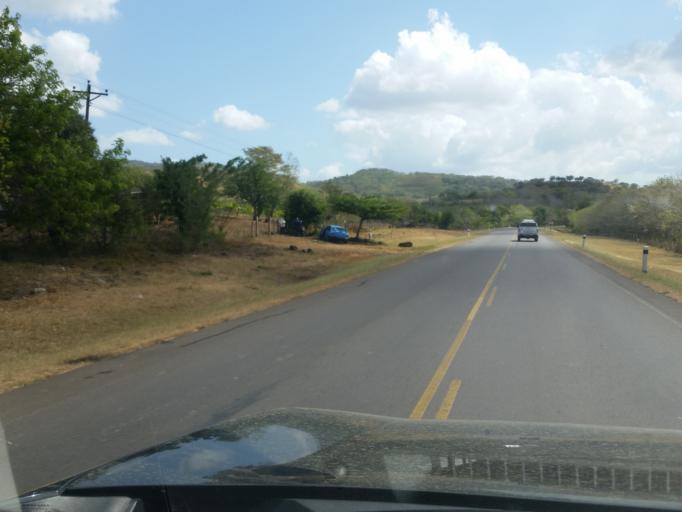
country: NI
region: Chontales
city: Comalapa
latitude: 12.2245
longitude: -85.6420
